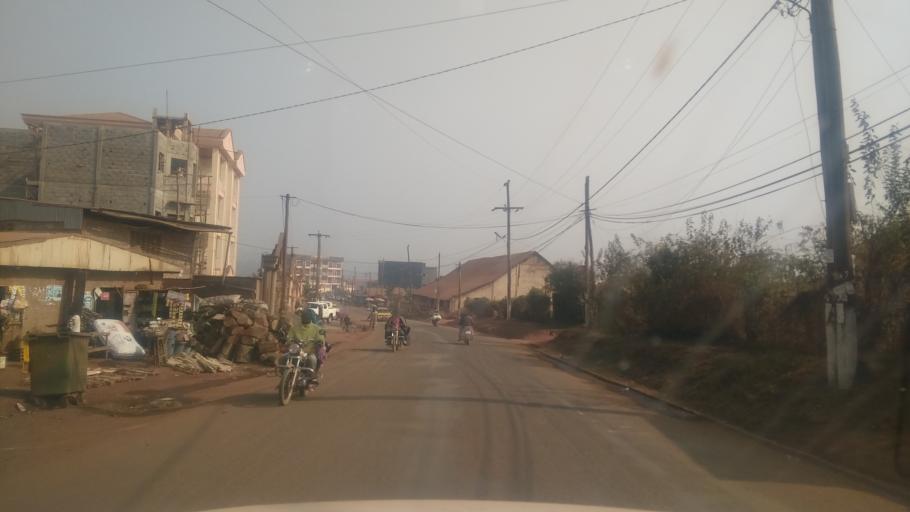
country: CM
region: West
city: Bafoussam
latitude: 5.5020
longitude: 10.3980
